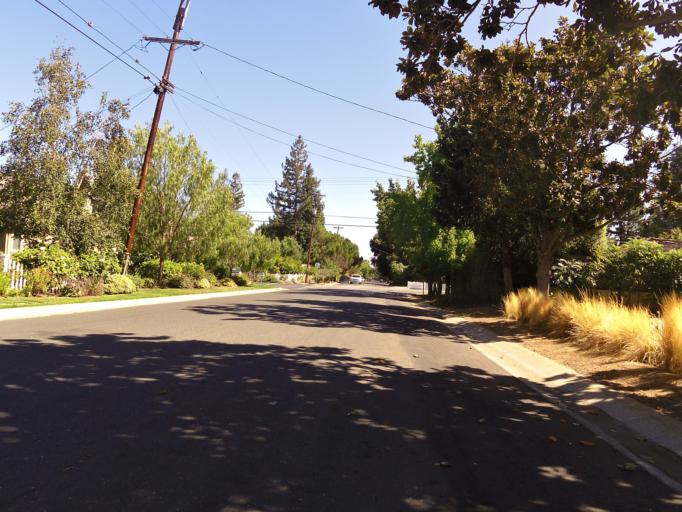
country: US
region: California
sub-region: Santa Clara County
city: Los Altos
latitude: 37.3920
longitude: -122.1087
